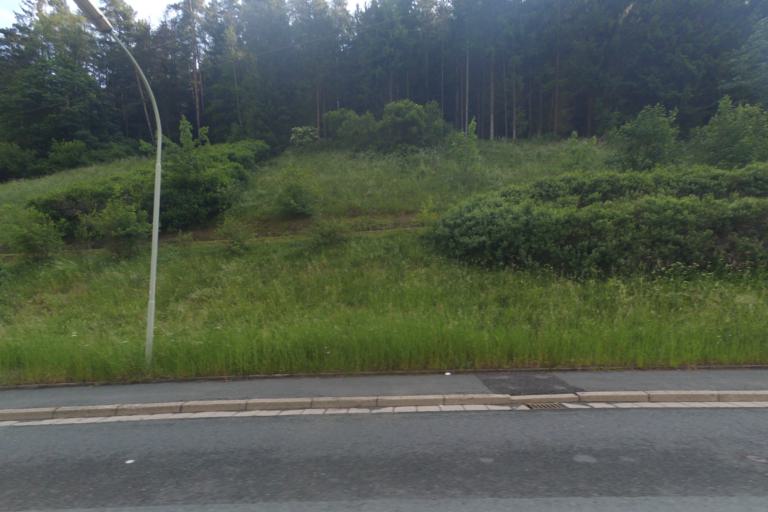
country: DE
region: Bavaria
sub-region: Upper Franconia
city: Ludwigsstadt
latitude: 50.4989
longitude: 11.3714
